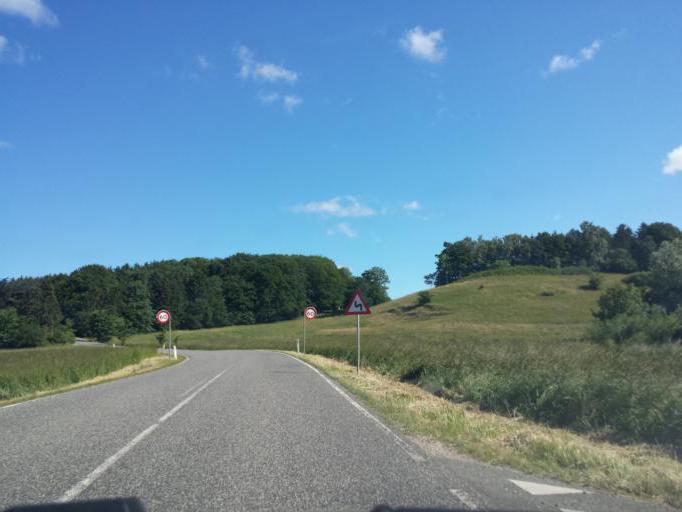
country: DK
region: Capital Region
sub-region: Egedal Kommune
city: Ganlose
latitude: 55.8030
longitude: 12.2645
